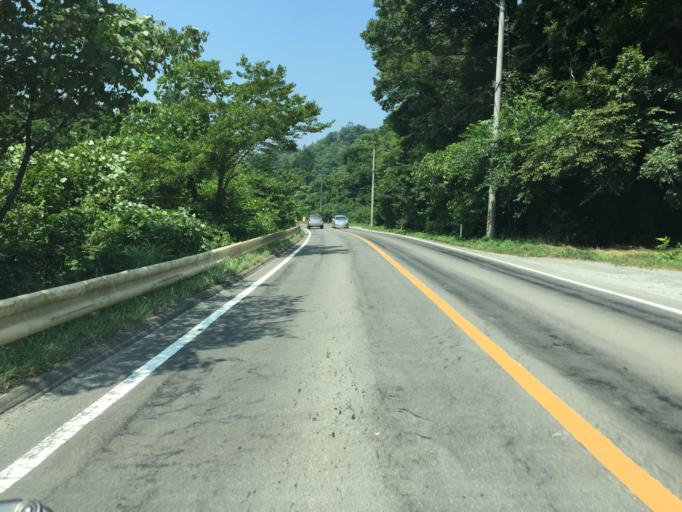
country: JP
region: Miyagi
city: Marumori
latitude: 37.8578
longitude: 140.8482
